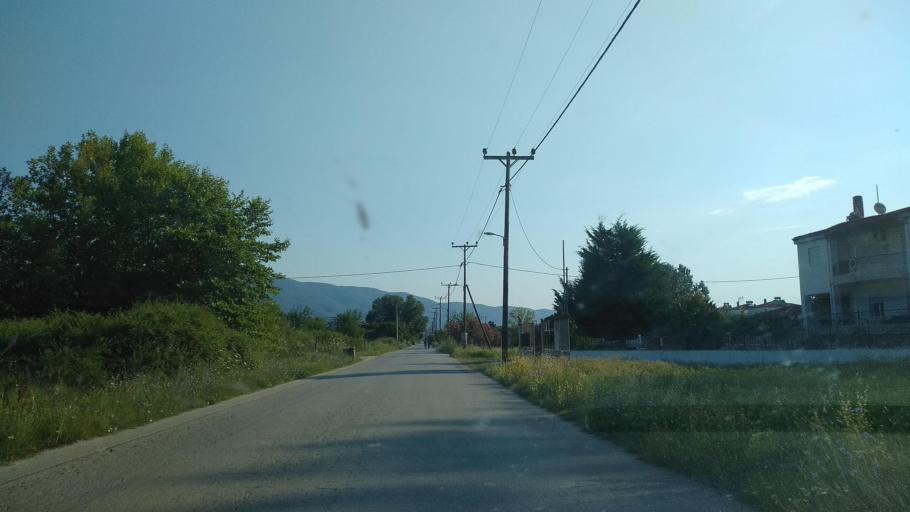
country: GR
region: Central Macedonia
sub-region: Nomos Thessalonikis
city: Stavros
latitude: 40.6825
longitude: 23.6875
